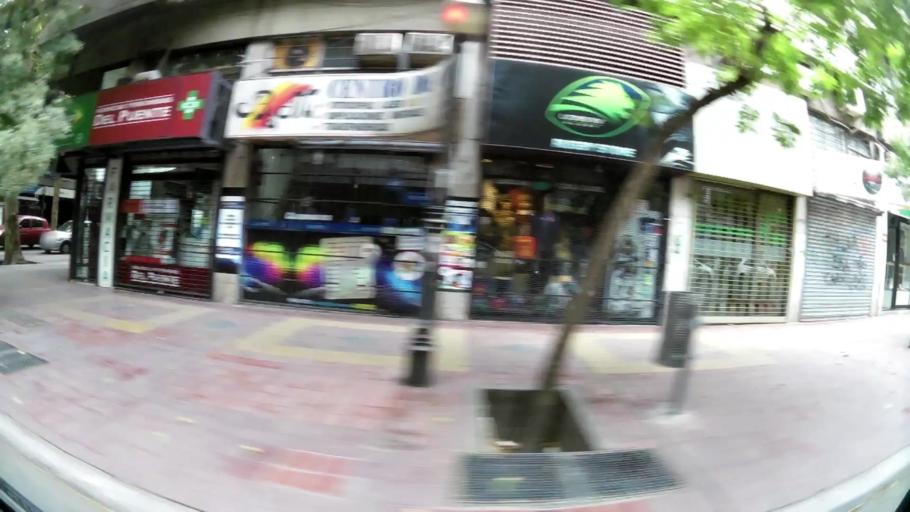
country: AR
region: Mendoza
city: Mendoza
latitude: -32.8890
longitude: -68.8420
